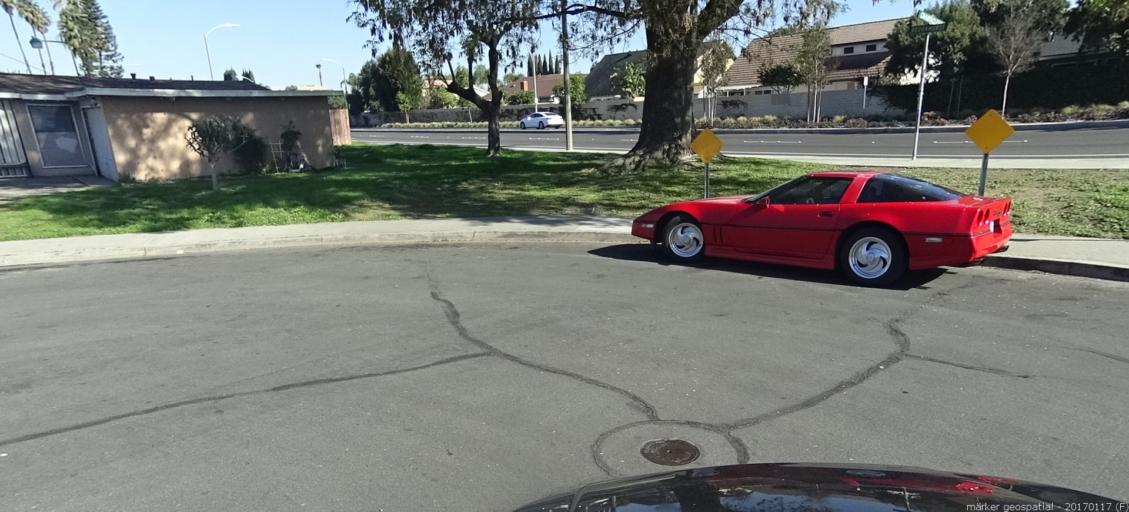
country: US
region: California
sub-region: Orange County
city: Stanton
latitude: 33.8127
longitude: -117.9592
